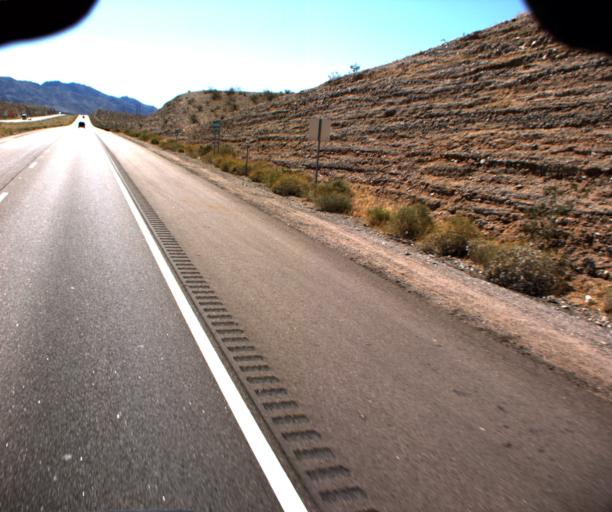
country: US
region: Nevada
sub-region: Clark County
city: Boulder City
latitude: 35.9658
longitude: -114.6722
